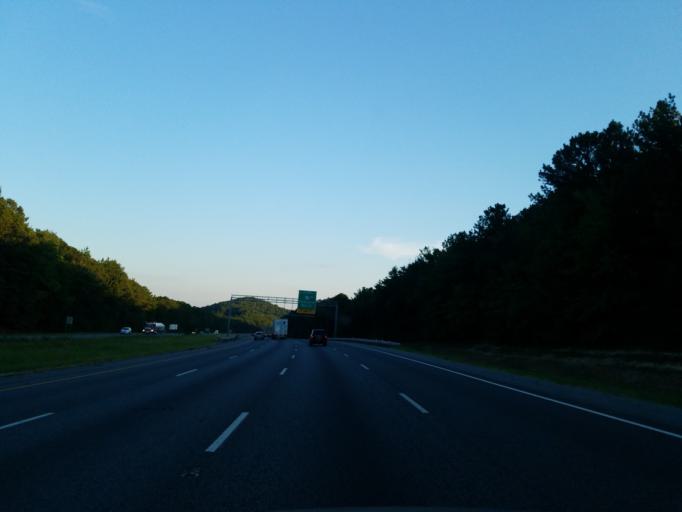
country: US
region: Georgia
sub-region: Bartow County
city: Cartersville
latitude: 34.1856
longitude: -84.7661
